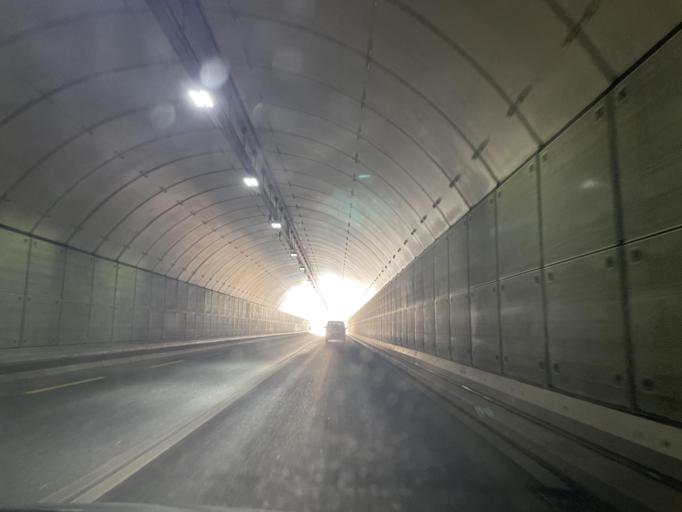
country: CH
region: Saint Gallen
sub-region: Wahlkreis Toggenburg
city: Krummenau
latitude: 47.2381
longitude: 9.1852
